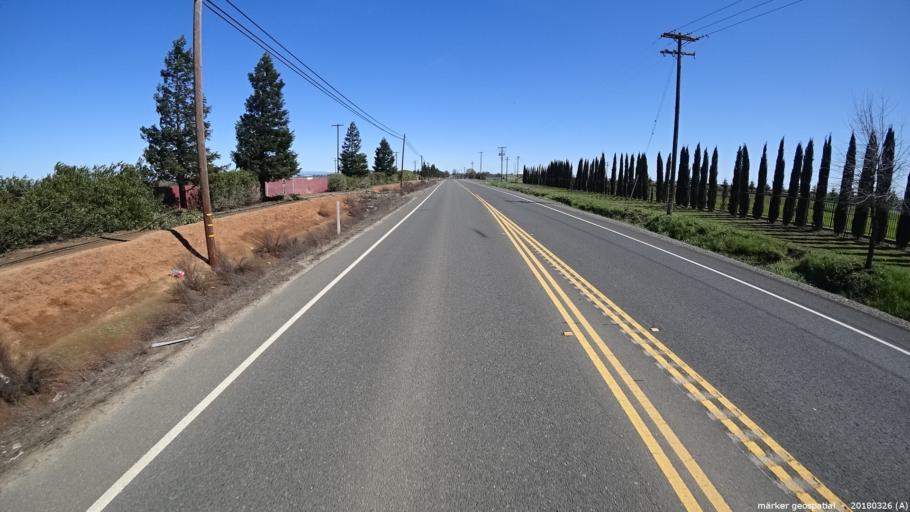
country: US
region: California
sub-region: Sacramento County
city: Rosemont
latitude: 38.5264
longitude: -121.3252
